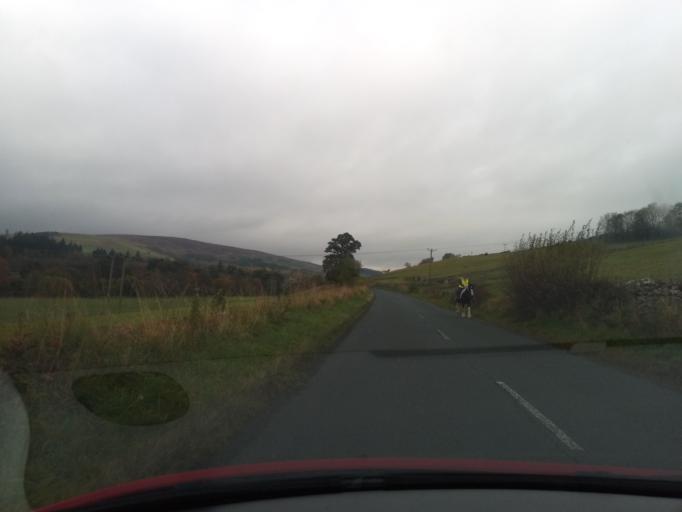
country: GB
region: Scotland
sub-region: The Scottish Borders
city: Selkirk
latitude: 55.6052
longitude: -2.8815
